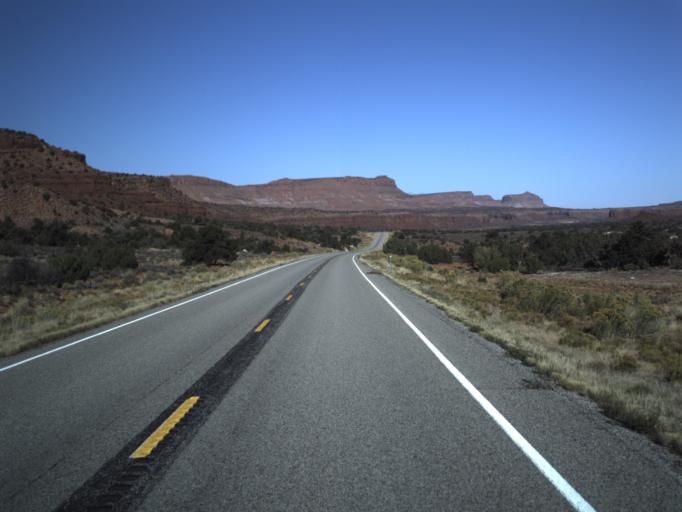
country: US
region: Utah
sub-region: San Juan County
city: Blanding
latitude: 37.6658
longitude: -110.1942
